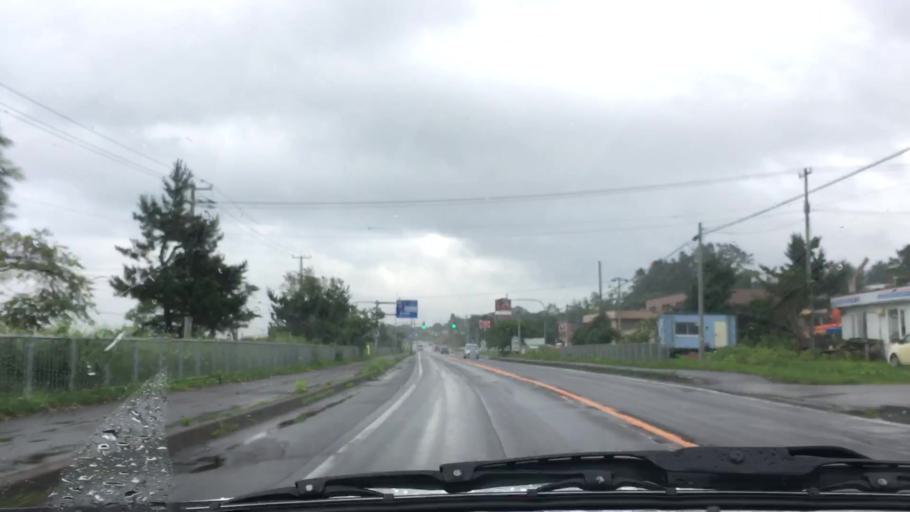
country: JP
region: Hokkaido
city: Nanae
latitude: 42.2364
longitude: 140.3085
